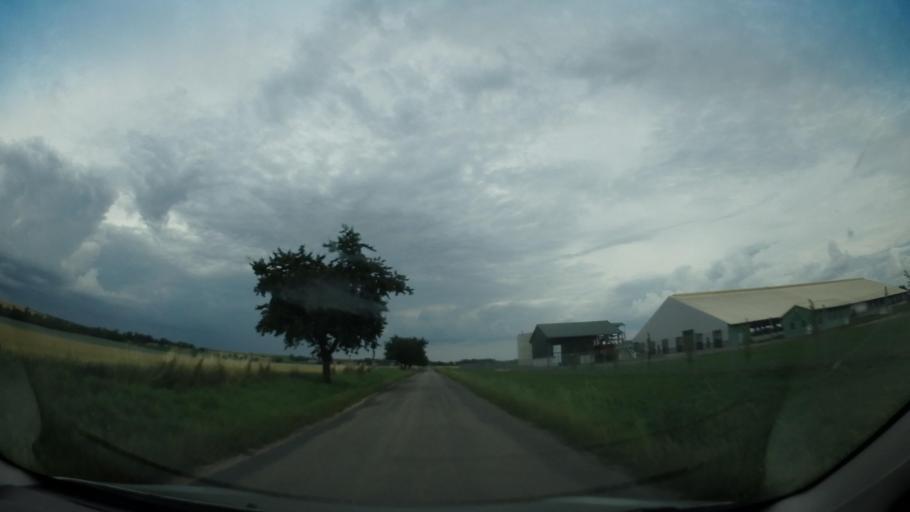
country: CZ
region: South Moravian
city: Ivanovice na Hane
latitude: 49.3203
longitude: 17.1240
